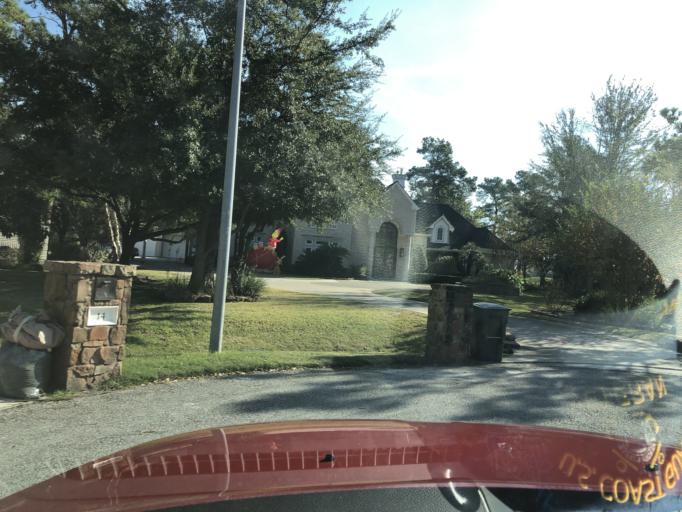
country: US
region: Texas
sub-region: Harris County
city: Tomball
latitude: 30.0400
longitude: -95.5569
